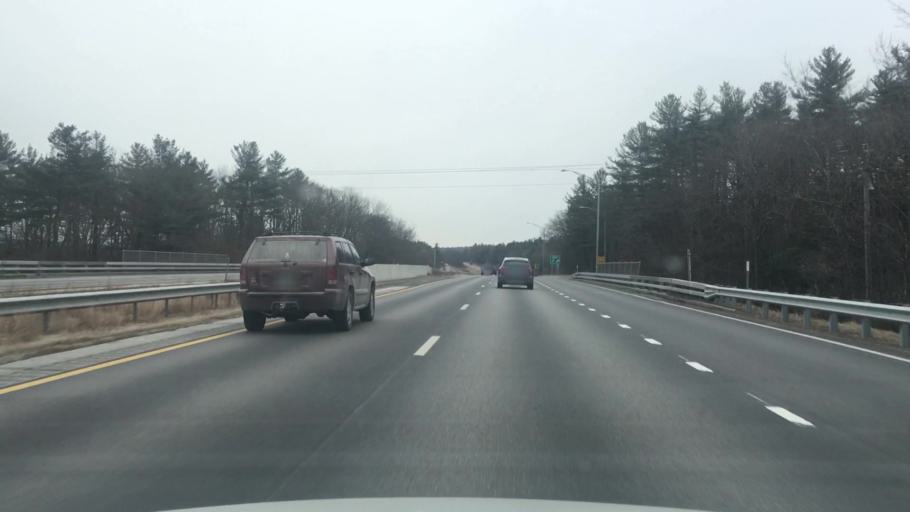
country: US
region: New Hampshire
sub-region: Merrimack County
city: Concord
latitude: 43.1802
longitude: -71.5678
